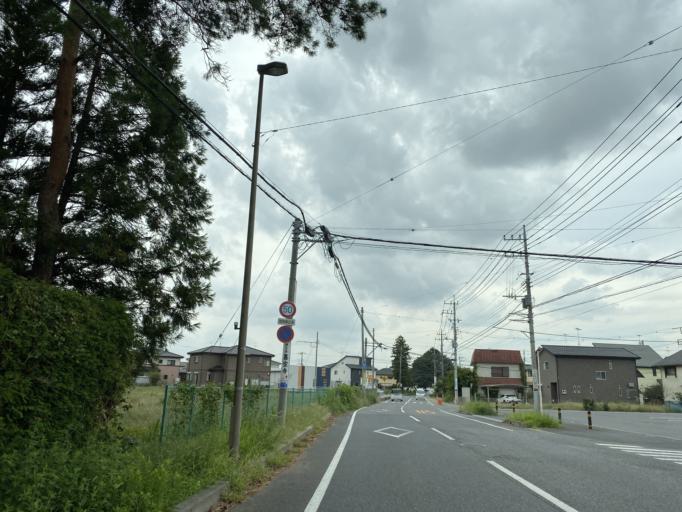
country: JP
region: Ibaraki
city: Mitsukaido
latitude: 35.9953
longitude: 140.0455
